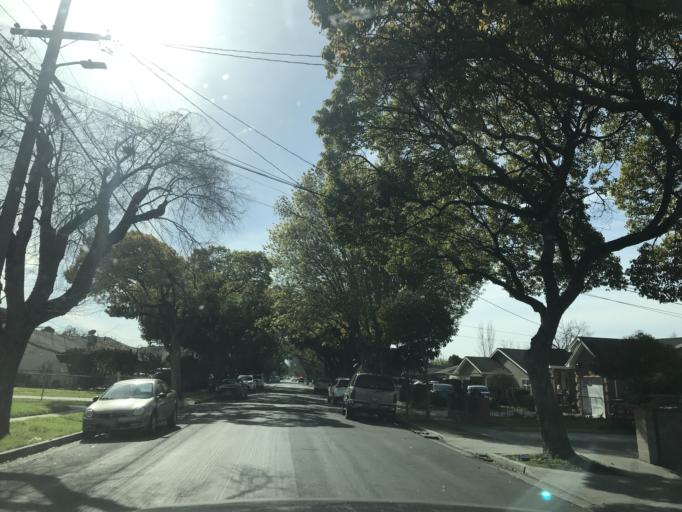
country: US
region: California
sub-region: San Mateo County
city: East Palo Alto
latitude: 37.4781
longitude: -122.1532
